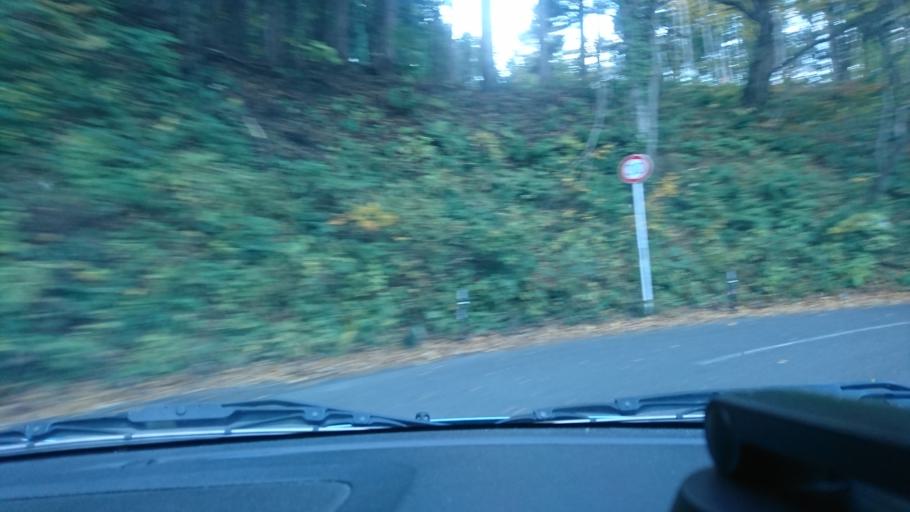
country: JP
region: Miyagi
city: Furukawa
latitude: 38.8623
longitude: 140.7759
